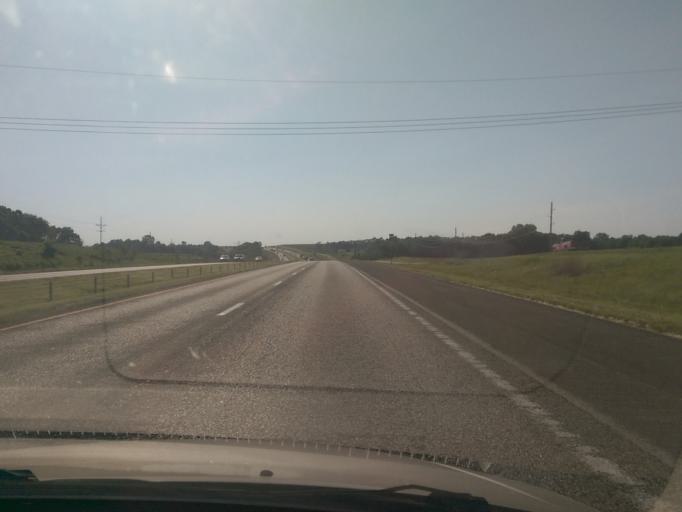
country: US
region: Missouri
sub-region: Lafayette County
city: Concordia
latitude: 38.9861
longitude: -93.5001
